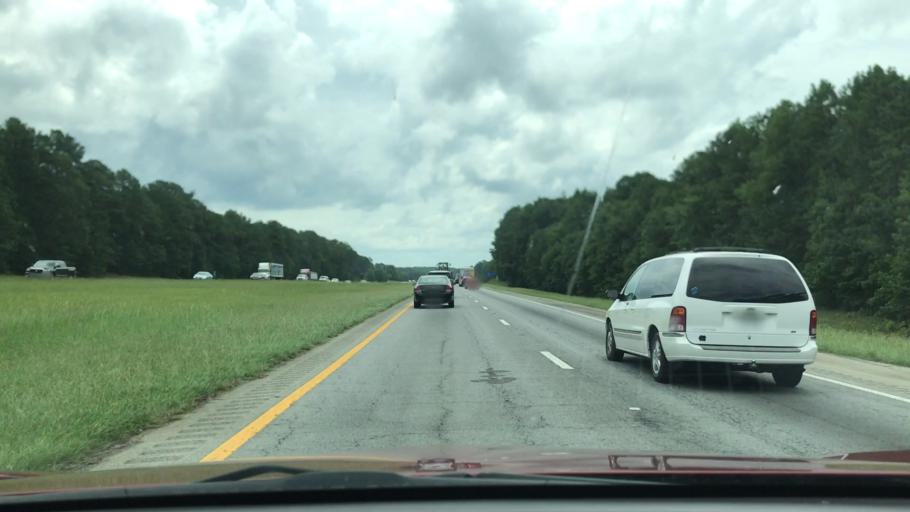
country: US
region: South Carolina
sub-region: Laurens County
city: Joanna
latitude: 34.4185
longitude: -81.7132
